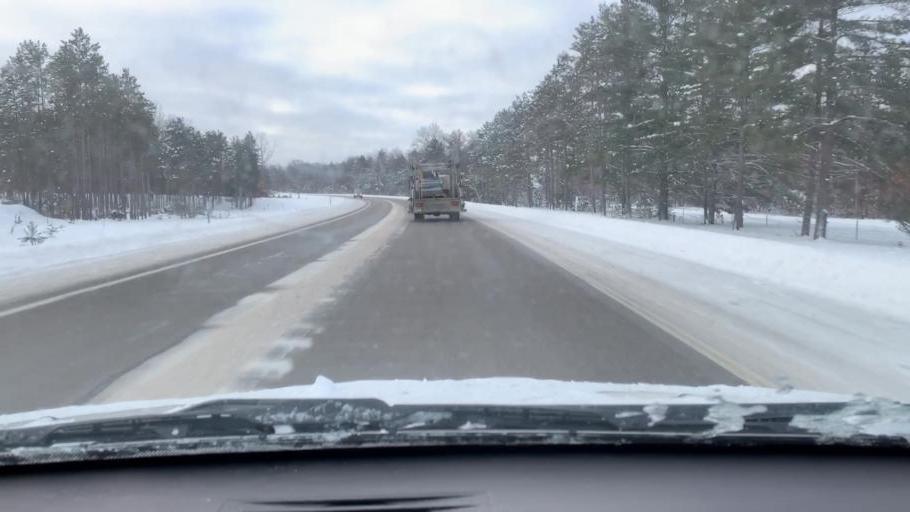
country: US
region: Michigan
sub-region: Wexford County
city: Manton
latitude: 44.5095
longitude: -85.4043
